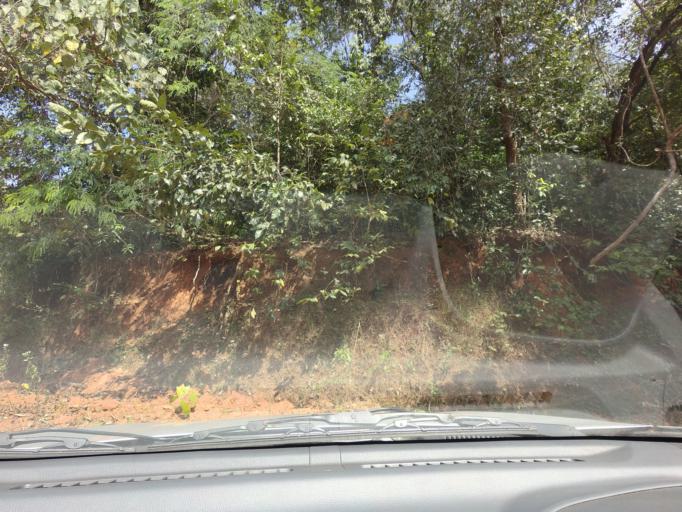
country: IN
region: Karnataka
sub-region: Kodagu
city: Somvarpet
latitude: 12.6907
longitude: 75.6180
